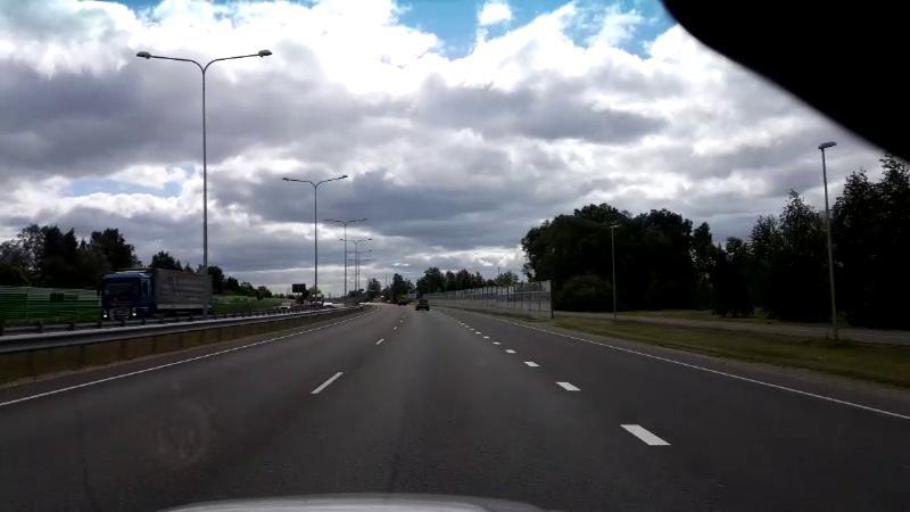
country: EE
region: Paernumaa
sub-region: Paernu linn
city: Parnu
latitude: 58.4001
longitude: 24.5120
